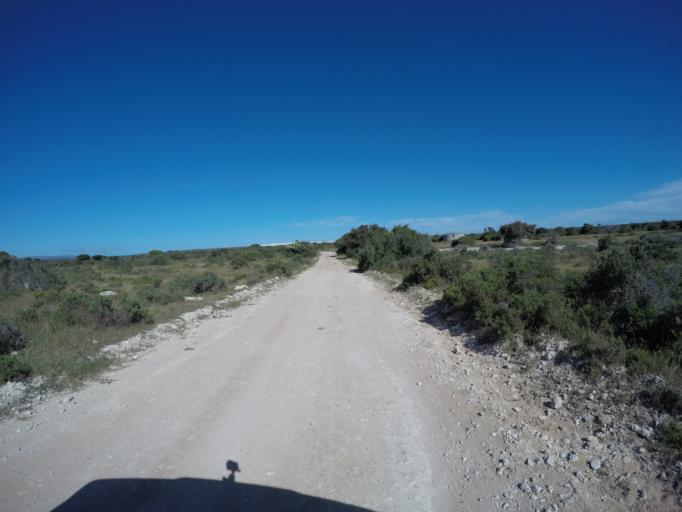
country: ZA
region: Western Cape
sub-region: Overberg District Municipality
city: Bredasdorp
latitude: -34.4554
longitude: 20.4100
